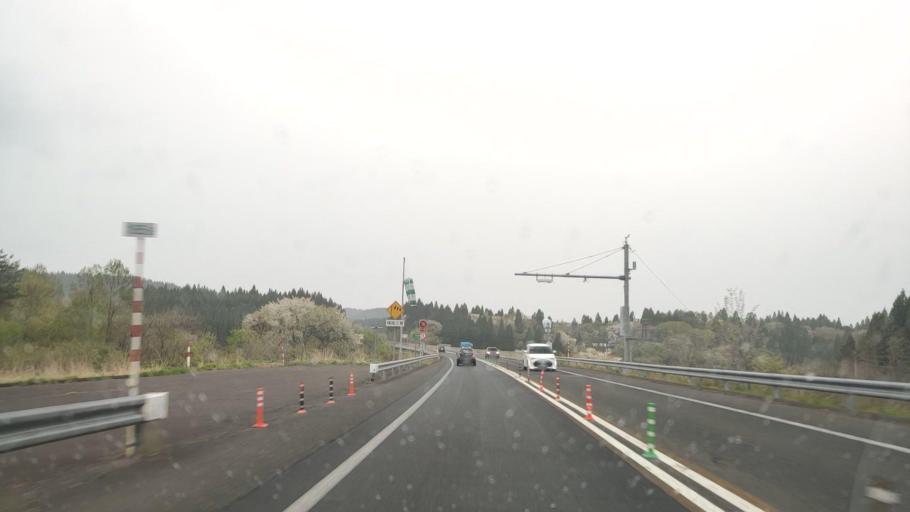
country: JP
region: Akita
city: Noshiromachi
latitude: 40.2088
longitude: 140.1857
